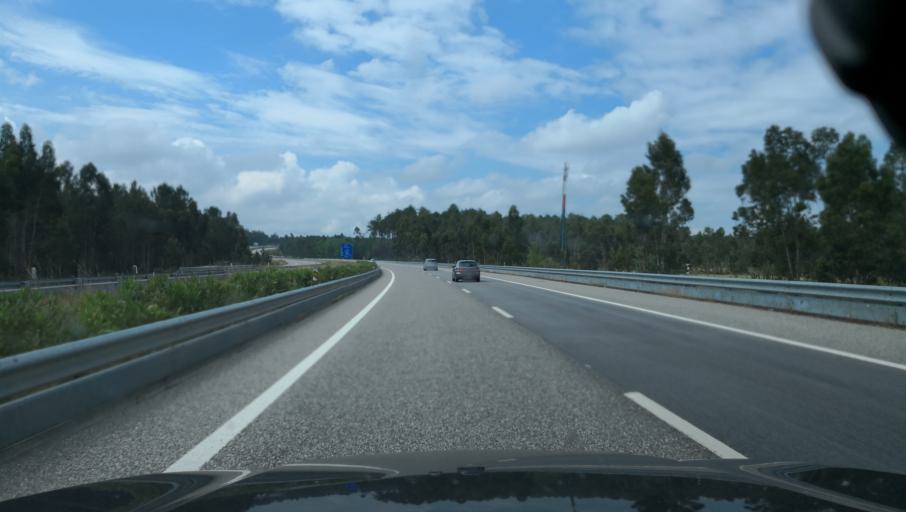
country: PT
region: Leiria
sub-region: Leiria
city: Amor
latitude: 39.7620
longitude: -8.8750
